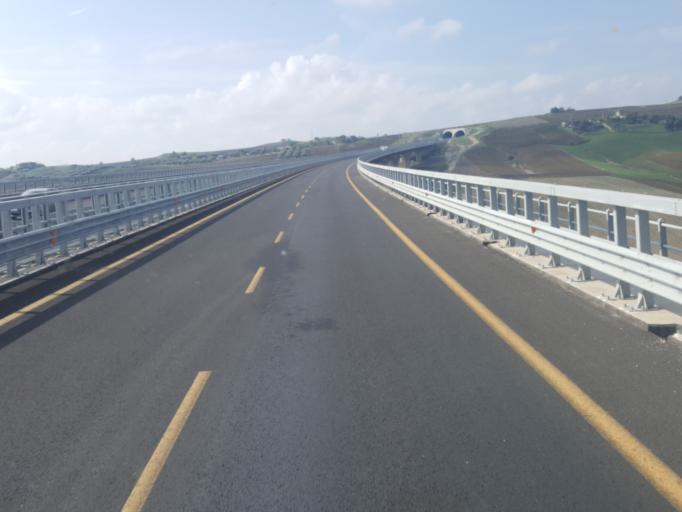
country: IT
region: Sicily
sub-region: Provincia di Caltanissetta
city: Serradifalco
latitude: 37.4314
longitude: 13.9349
